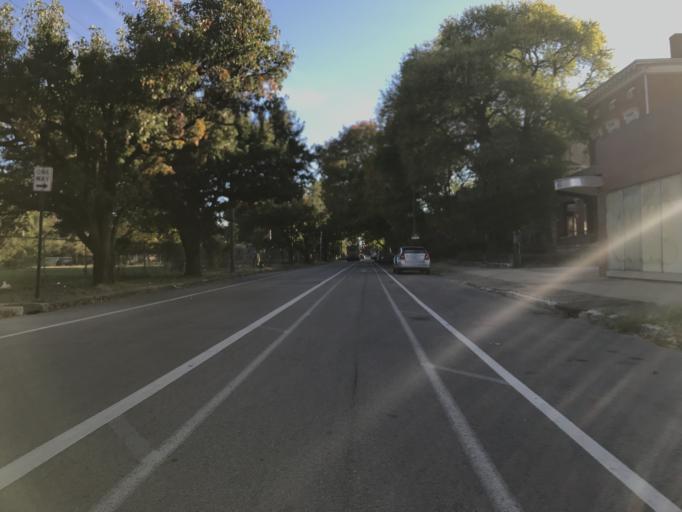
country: US
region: Kentucky
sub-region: Jefferson County
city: Louisville
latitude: 38.2419
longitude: -85.7625
